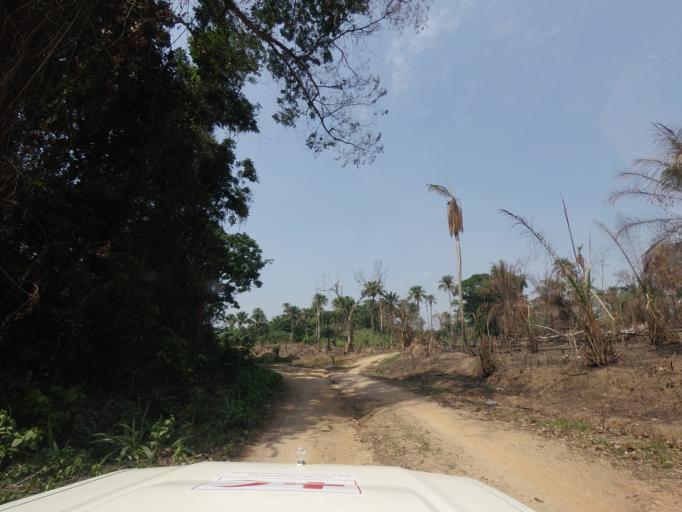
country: LR
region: Lofa
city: Voinjama
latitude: 8.5126
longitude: -9.6335
